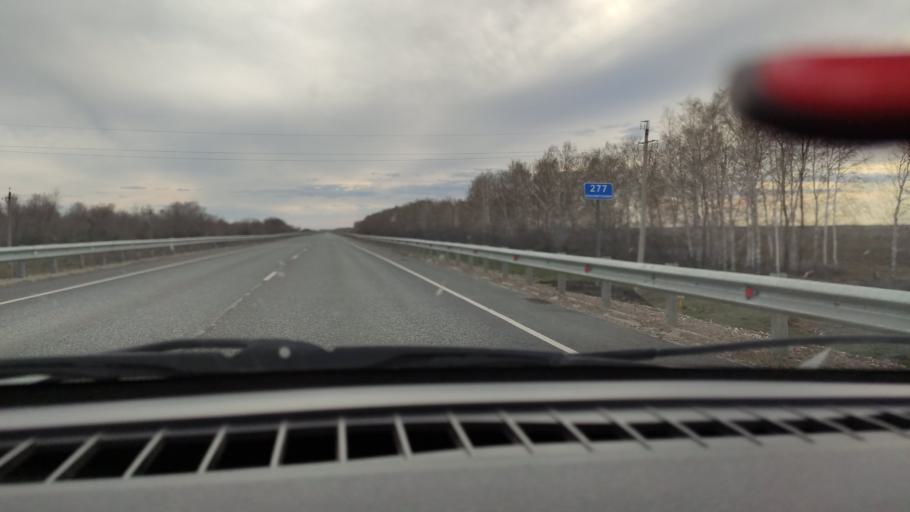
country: RU
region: Bashkortostan
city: Mayachnyy
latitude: 52.4066
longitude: 55.7318
